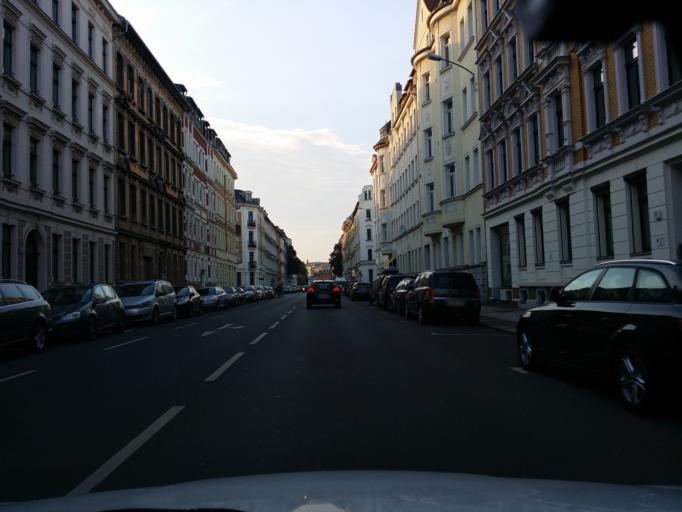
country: DE
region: Saxony
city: Leipzig
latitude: 51.3242
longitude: 12.3439
